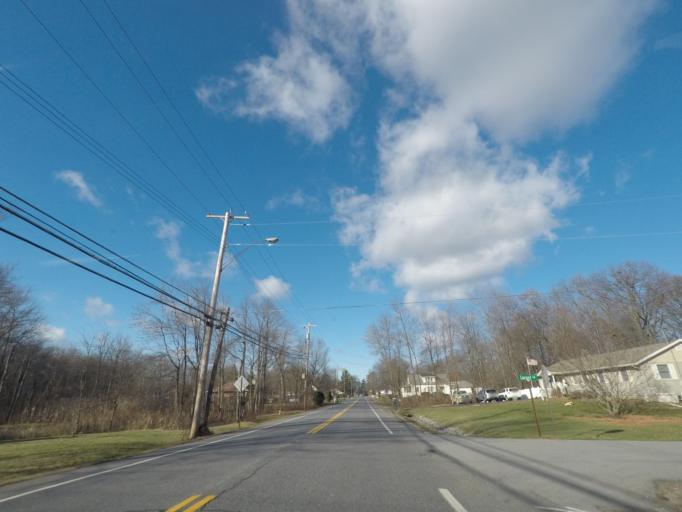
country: US
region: New York
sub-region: Saratoga County
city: Waterford
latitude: 42.8352
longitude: -73.7310
